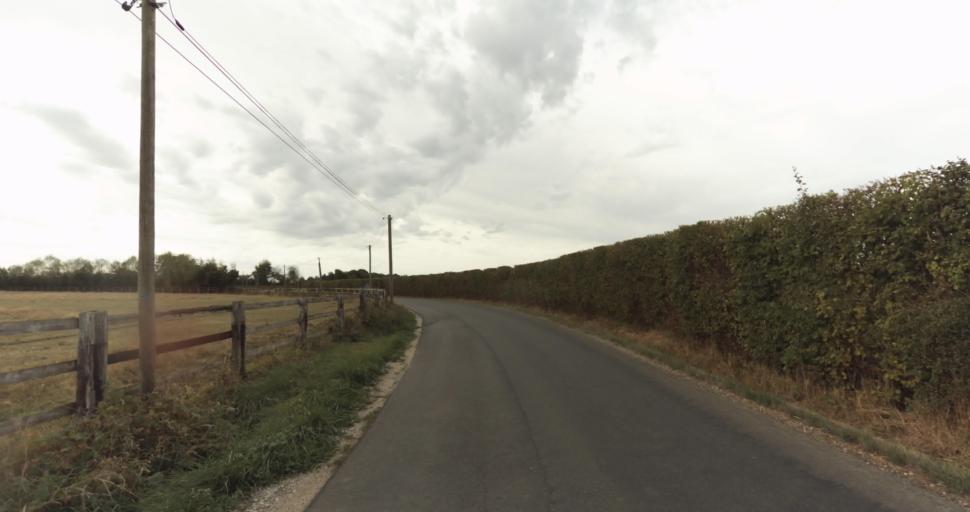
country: FR
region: Lower Normandy
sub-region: Departement du Calvados
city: La Vespiere
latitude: 48.9315
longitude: 0.3437
